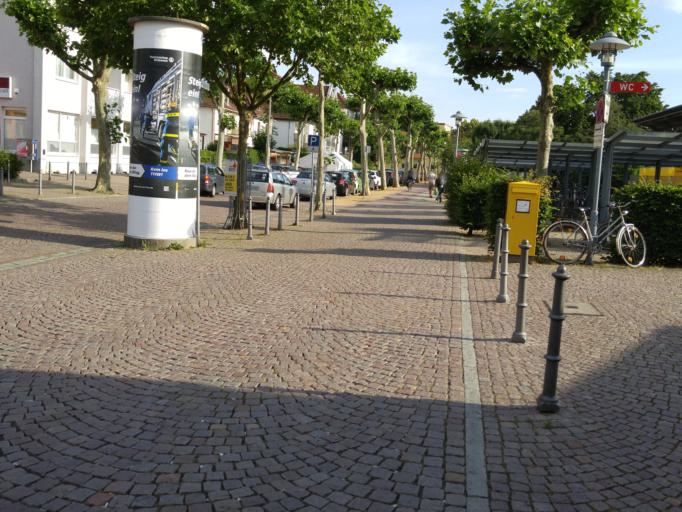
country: DE
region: Hesse
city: Langen
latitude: 49.9934
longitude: 8.6574
